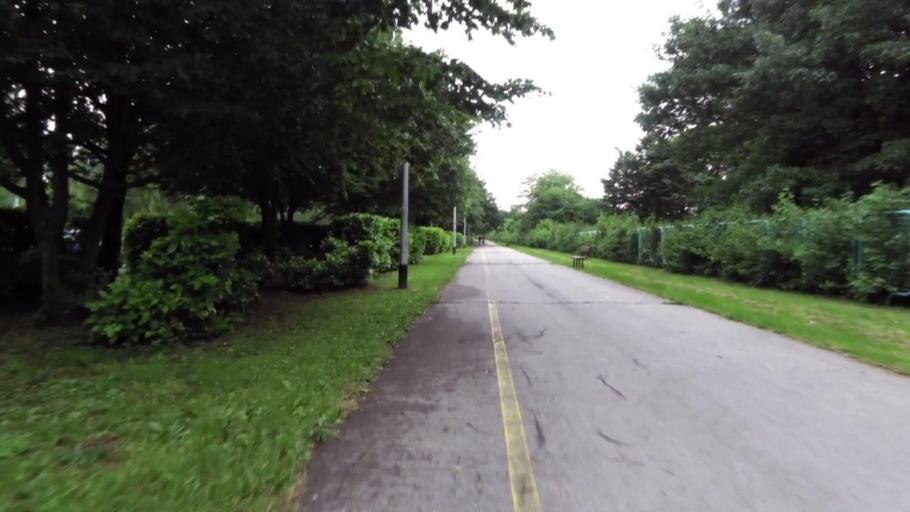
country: HR
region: Grad Zagreb
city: Dubrava
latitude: 45.8351
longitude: 16.0335
